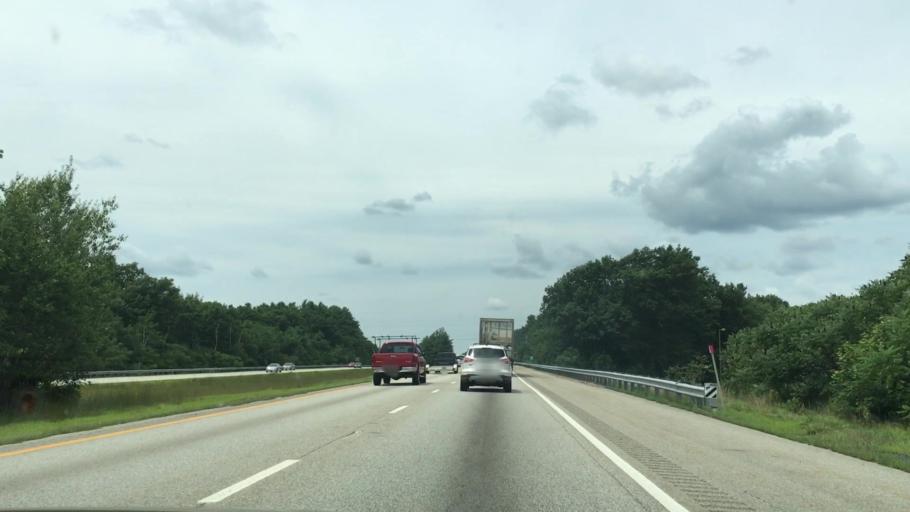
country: US
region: Massachusetts
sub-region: Worcester County
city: Westminster
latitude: 42.5540
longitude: -71.9179
